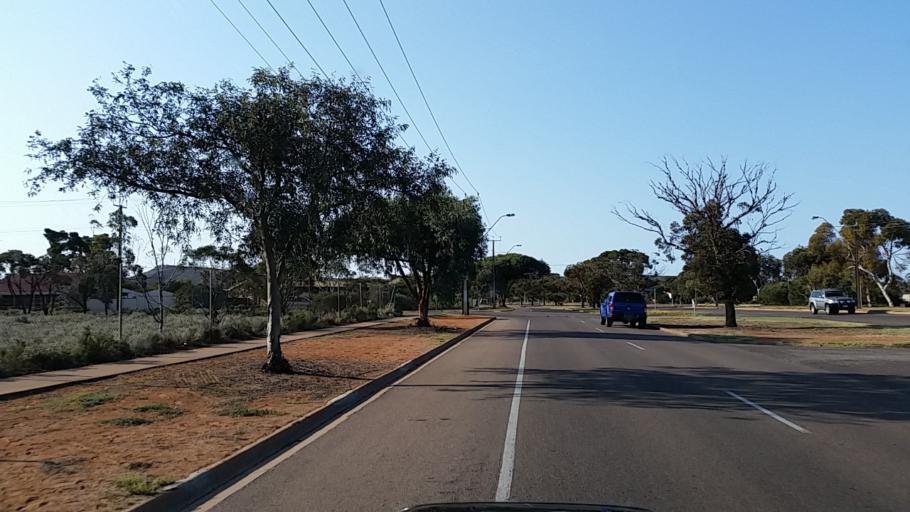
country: AU
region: South Australia
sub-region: Whyalla
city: Whyalla
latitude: -33.0243
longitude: 137.5312
